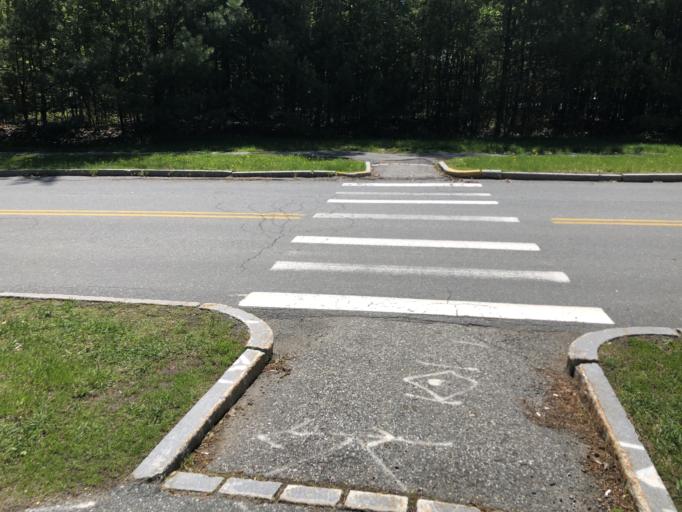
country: US
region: New Hampshire
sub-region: Grafton County
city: Lebanon
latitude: 43.6789
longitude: -72.2601
